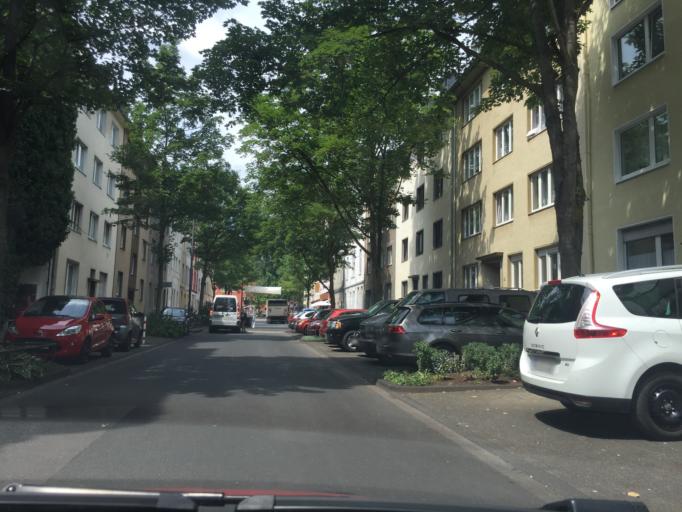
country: DE
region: North Rhine-Westphalia
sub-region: Regierungsbezirk Koln
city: Neustadt/Sued
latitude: 50.9129
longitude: 6.9428
